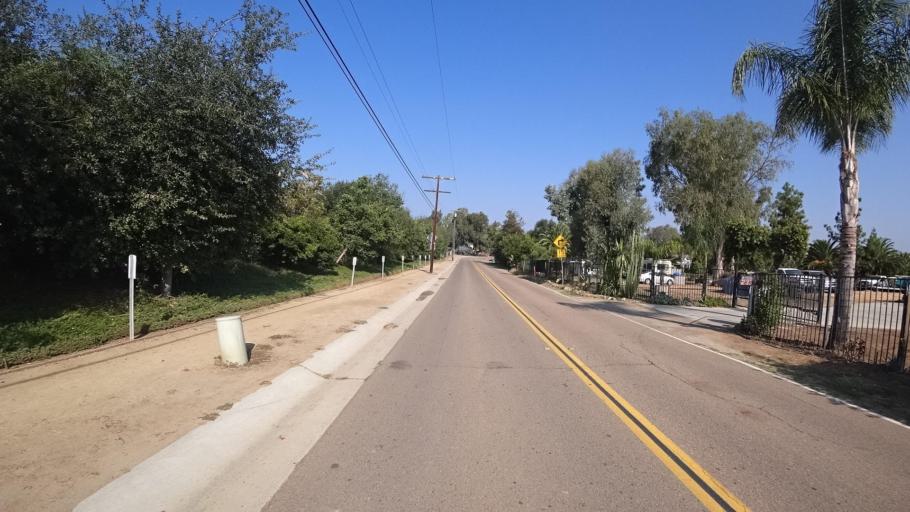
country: US
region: California
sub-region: San Diego County
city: Vista
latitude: 33.2369
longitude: -117.2539
